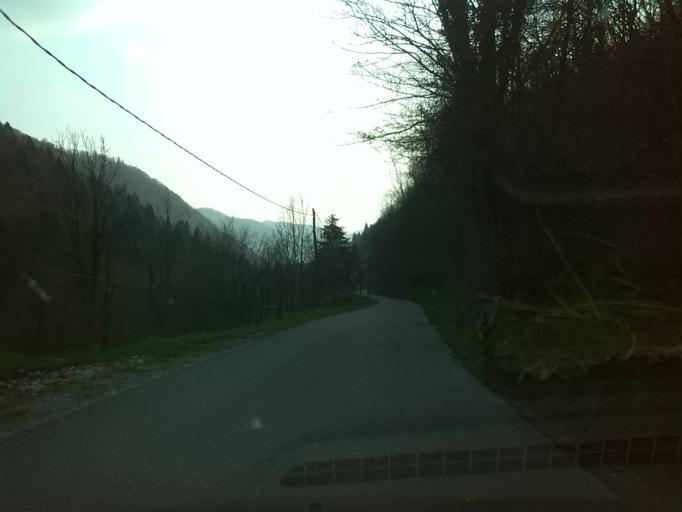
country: IT
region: Friuli Venezia Giulia
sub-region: Provincia di Udine
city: Cras
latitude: 46.1938
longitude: 13.5911
